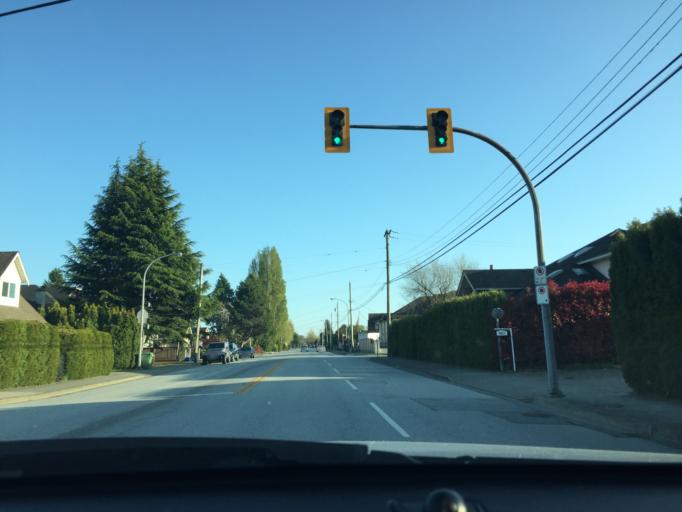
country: CA
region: British Columbia
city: Richmond
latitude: 49.1521
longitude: -123.1253
